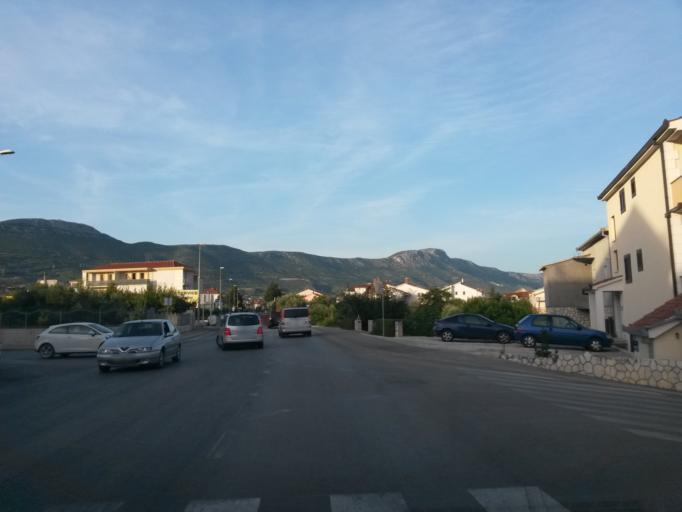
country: HR
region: Splitsko-Dalmatinska
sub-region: Grad Trogir
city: Trogir
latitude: 43.5475
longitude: 16.3240
